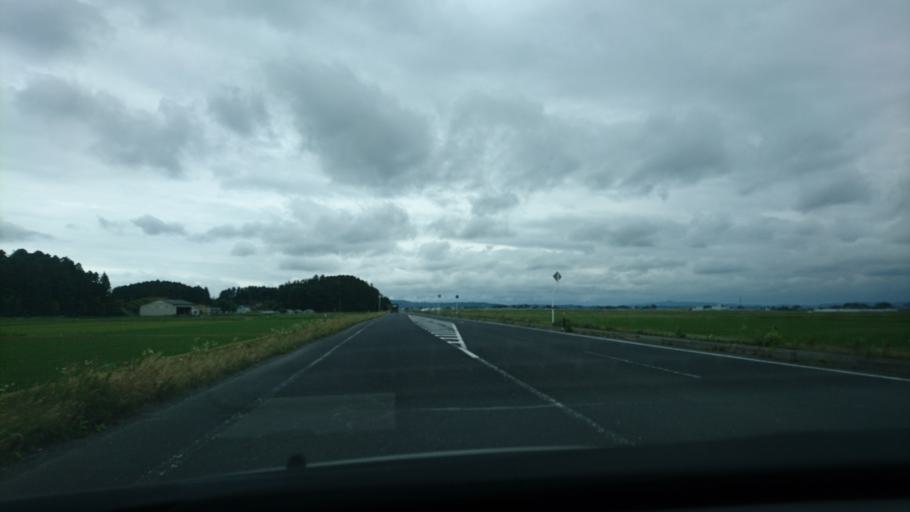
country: JP
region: Miyagi
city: Wakuya
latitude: 38.6992
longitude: 141.2603
